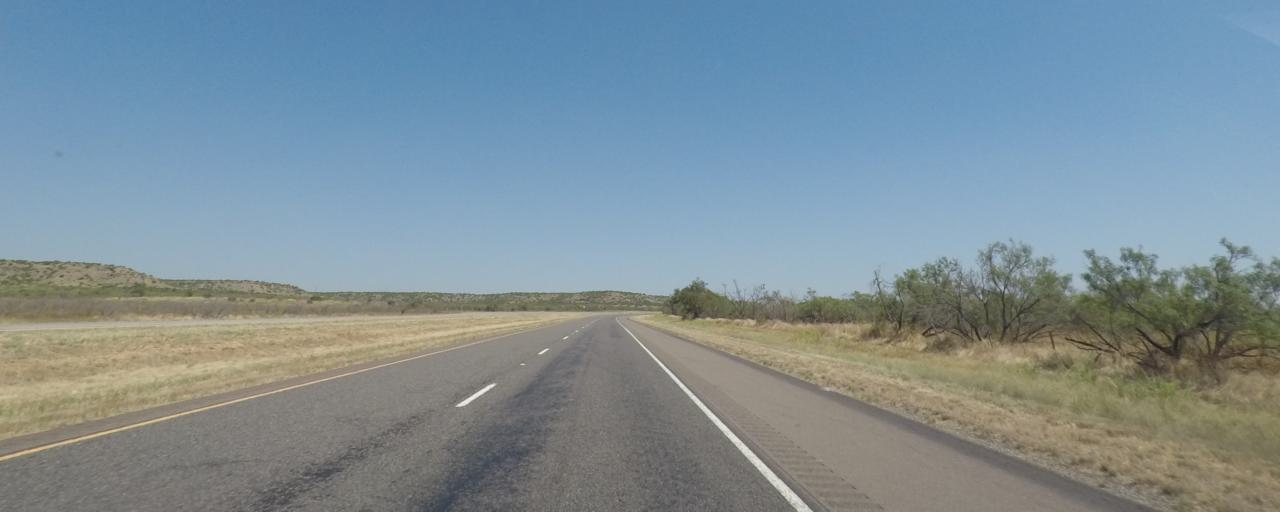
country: US
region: Texas
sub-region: Dickens County
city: Dickens
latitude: 33.6336
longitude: -100.8832
